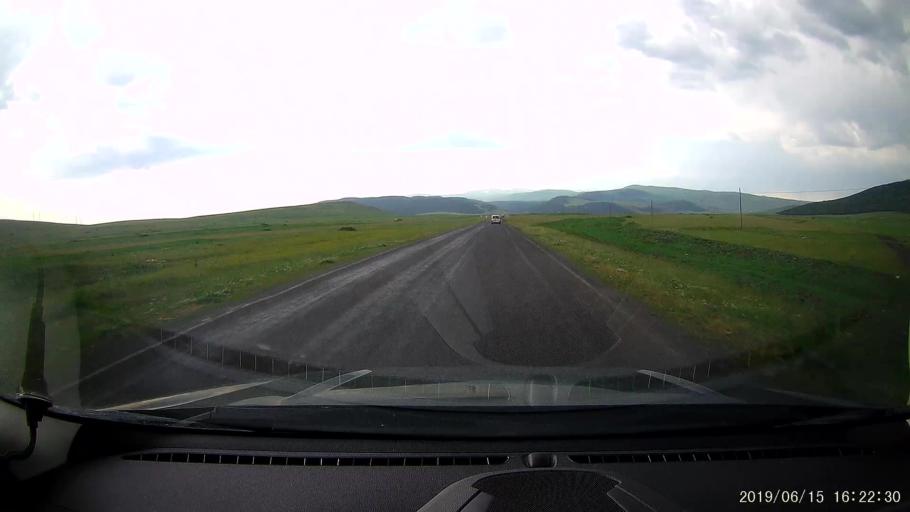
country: TR
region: Ardahan
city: Hanak
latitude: 41.1875
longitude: 42.8513
